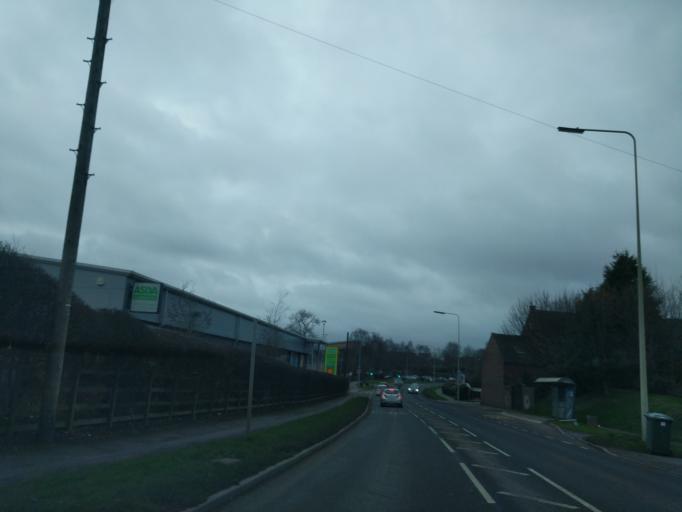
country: GB
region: England
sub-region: Staffordshire
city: Cannock
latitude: 52.6867
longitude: -2.0180
